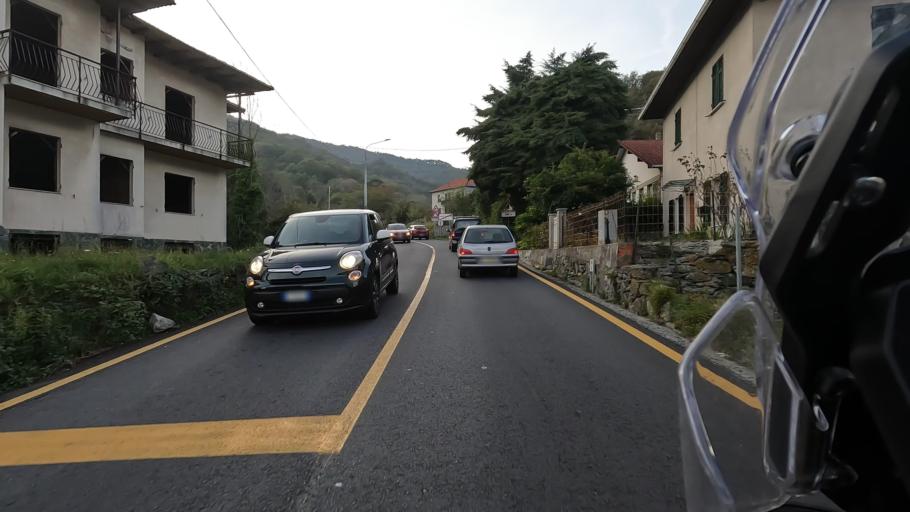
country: IT
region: Liguria
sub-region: Provincia di Savona
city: Osteria dei Cacciatori-Stella
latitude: 44.4186
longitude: 8.4796
